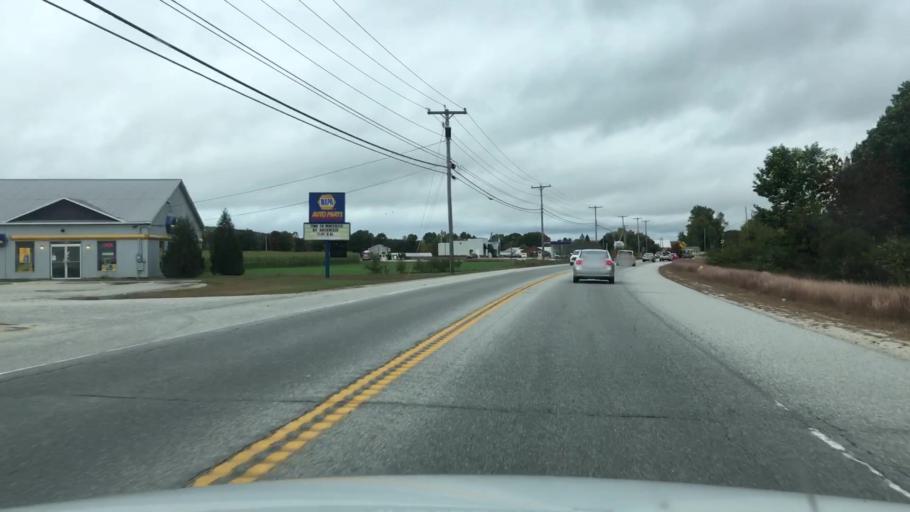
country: US
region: Maine
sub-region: Oxford County
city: South Paris
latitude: 44.1784
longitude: -70.5151
